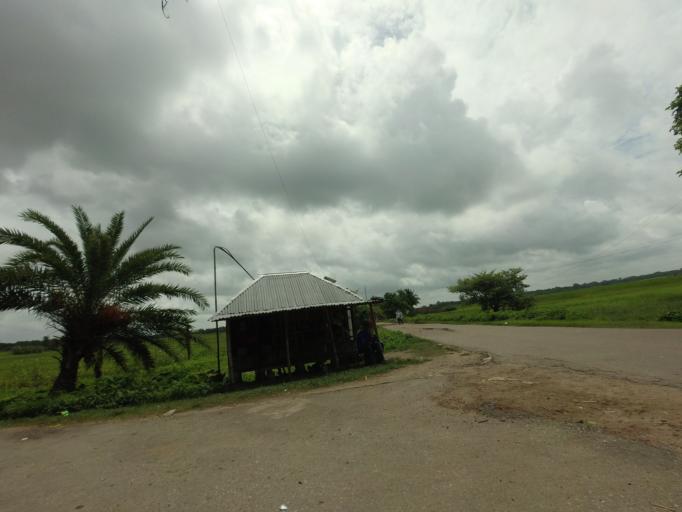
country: BD
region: Khulna
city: Kalia
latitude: 23.0406
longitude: 89.6451
